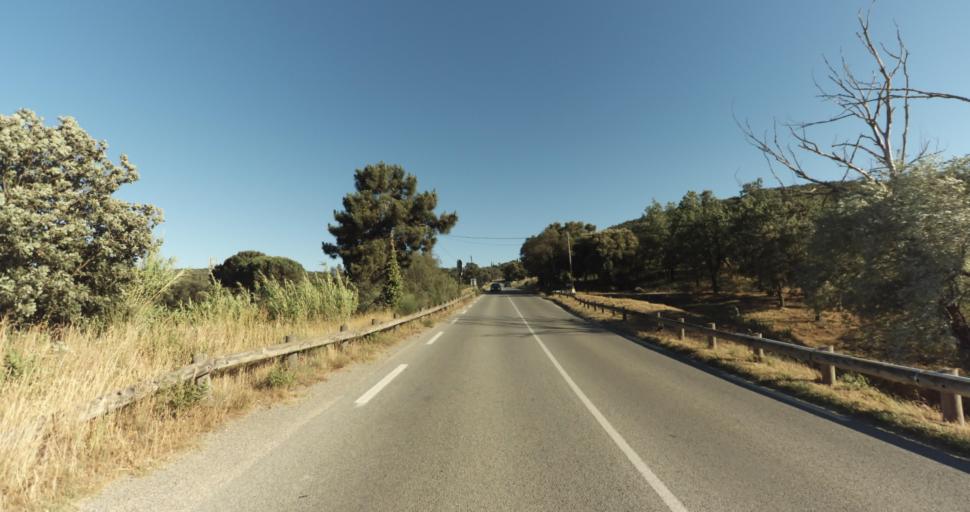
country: FR
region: Provence-Alpes-Cote d'Azur
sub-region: Departement du Var
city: Ramatuelle
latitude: 43.2353
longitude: 6.6105
